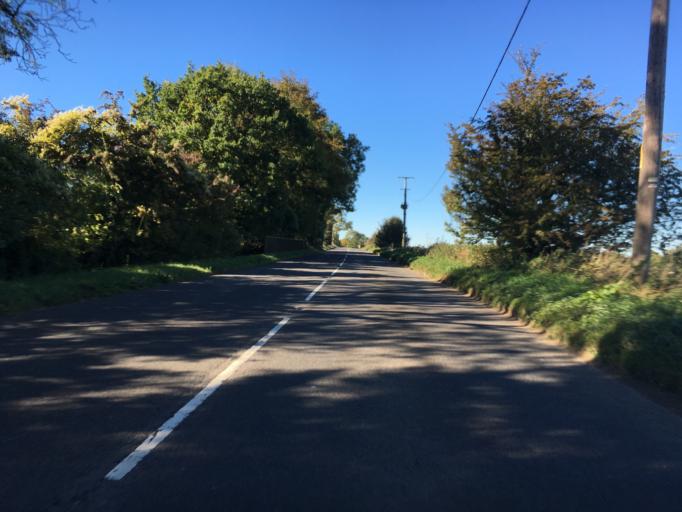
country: GB
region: England
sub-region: Wiltshire
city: Colerne
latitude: 51.4691
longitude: -2.2680
